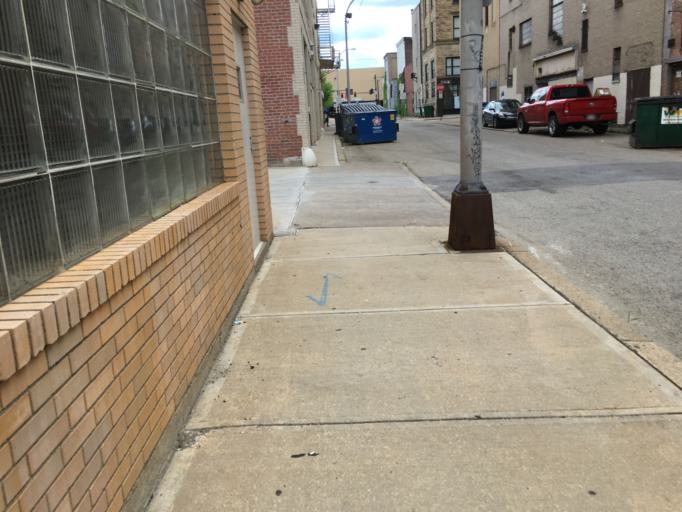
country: US
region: Pennsylvania
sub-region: Allegheny County
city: Bloomfield
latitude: 40.4618
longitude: -79.9240
